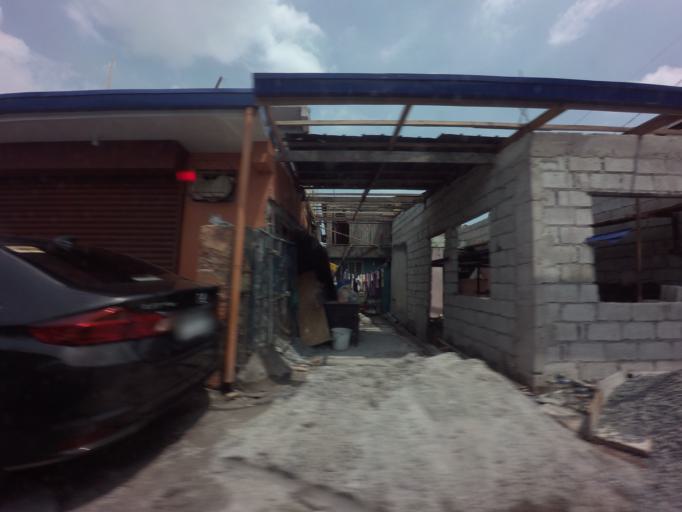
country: PH
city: Sambayanihan People's Village
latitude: 14.4638
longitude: 121.0552
